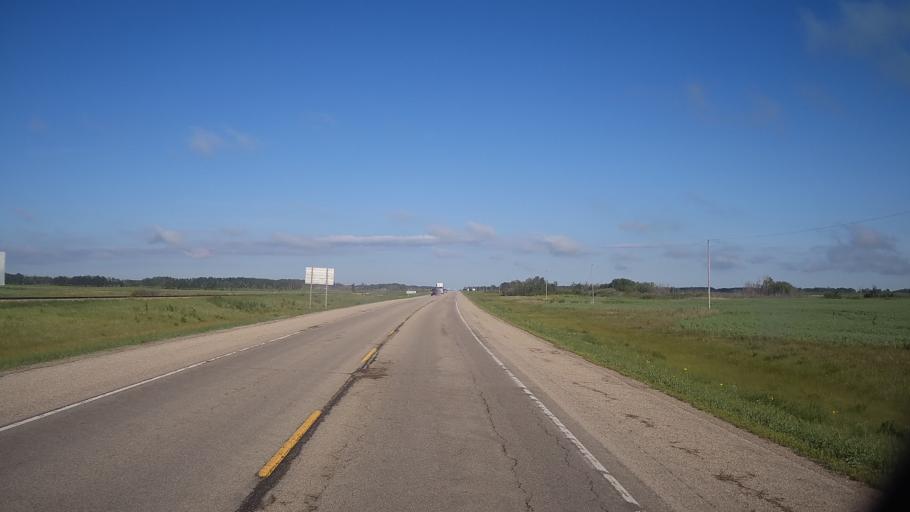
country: CA
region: Saskatchewan
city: Lanigan
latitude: 51.8503
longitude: -105.0604
